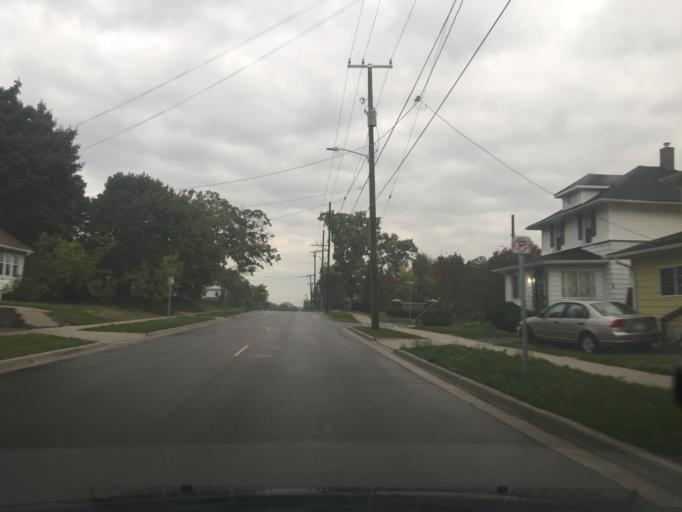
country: US
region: Michigan
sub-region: Oakland County
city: Pontiac
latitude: 42.6303
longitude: -83.2821
